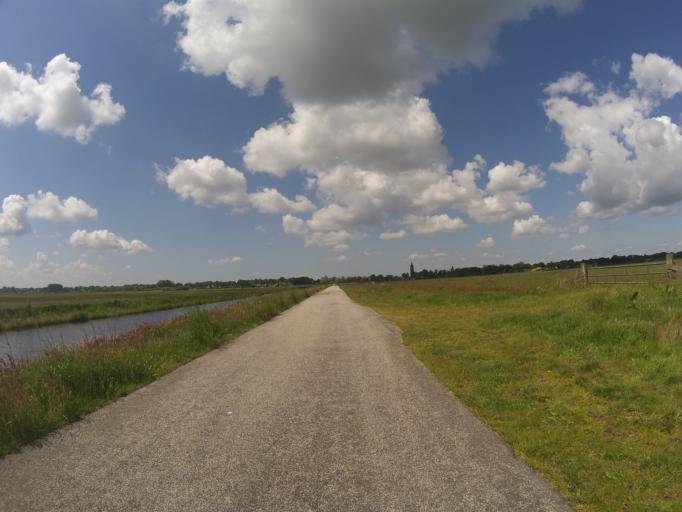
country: NL
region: Utrecht
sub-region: Gemeente Baarn
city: Baarn
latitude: 52.2494
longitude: 5.2781
